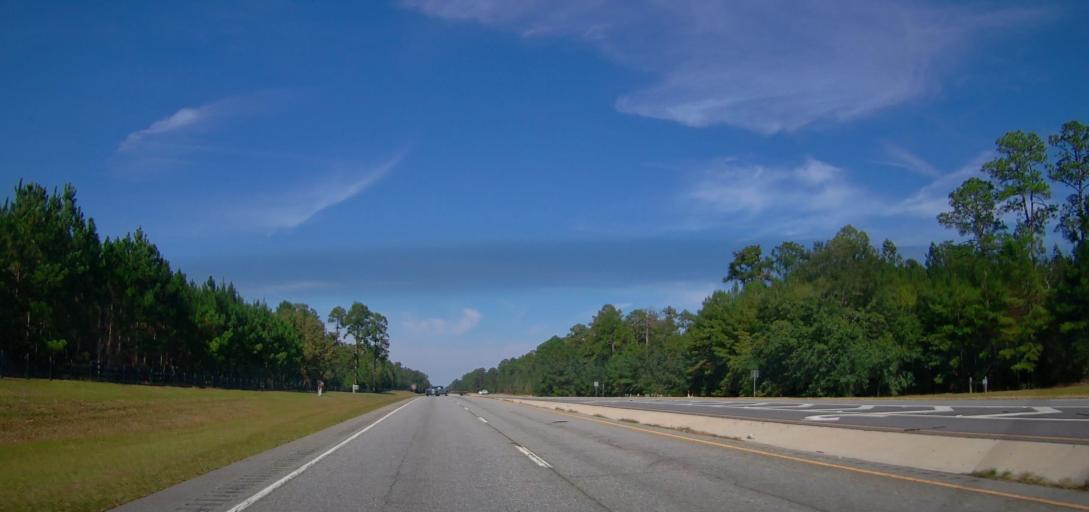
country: US
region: Georgia
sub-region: Lee County
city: Leesburg
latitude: 31.6747
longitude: -83.9956
